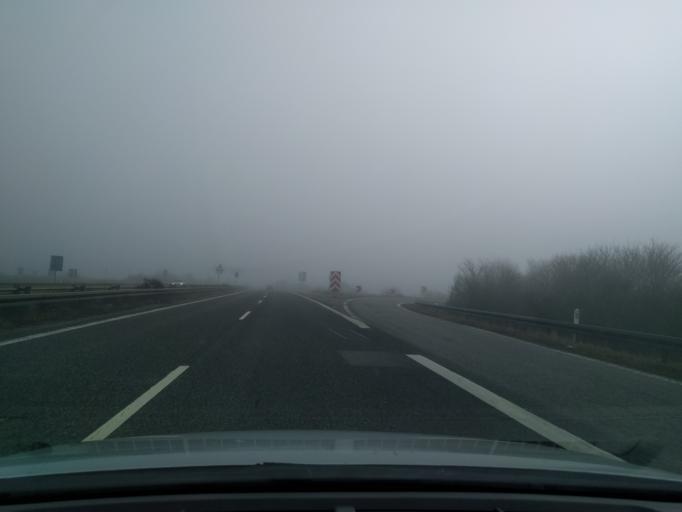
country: DK
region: Zealand
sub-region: Slagelse Kommune
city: Korsor
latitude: 55.3518
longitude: 11.1418
